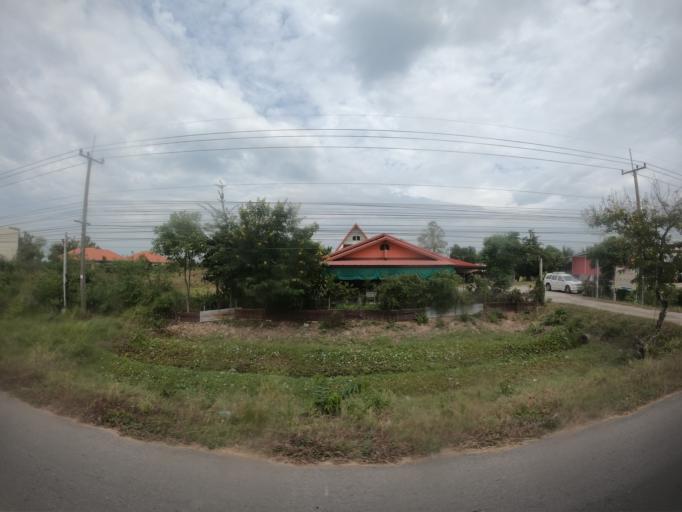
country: TH
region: Maha Sarakham
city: Maha Sarakham
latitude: 16.1595
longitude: 103.3588
